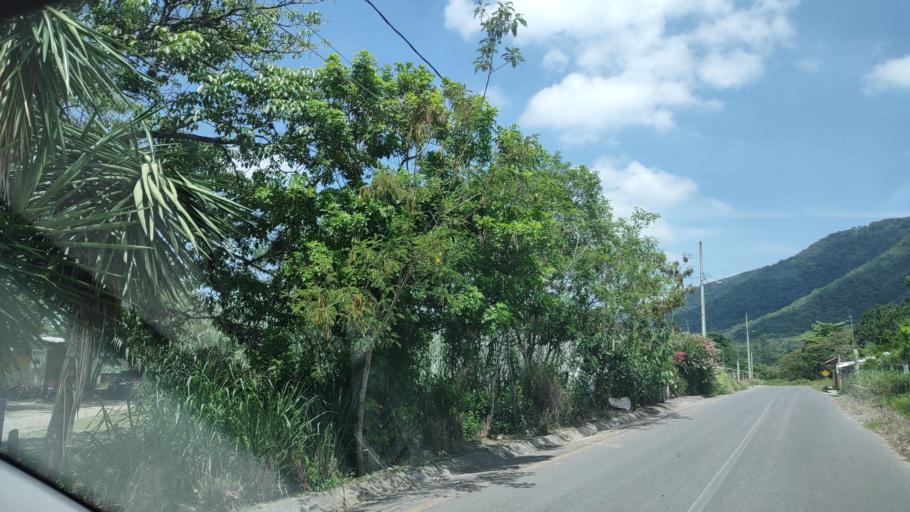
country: MX
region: Veracruz
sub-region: Emiliano Zapata
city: Dos Rios
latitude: 19.4273
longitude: -96.8060
